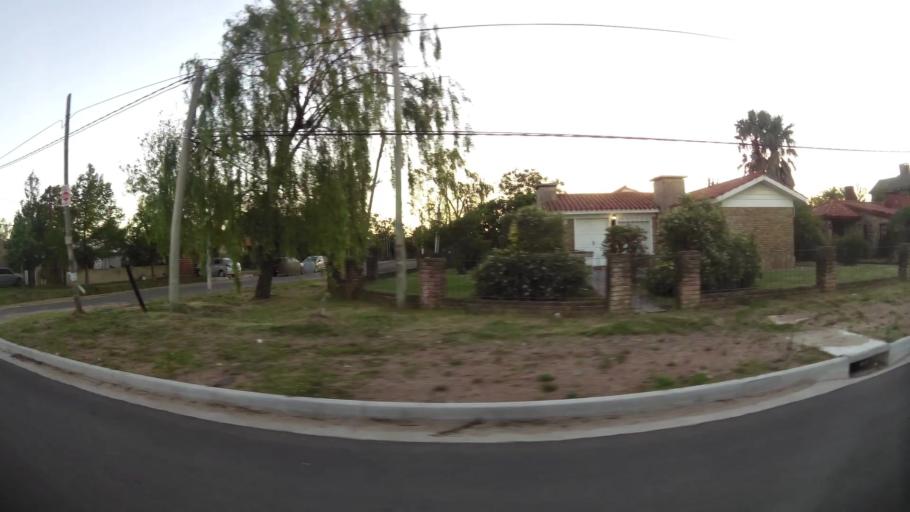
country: UY
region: Canelones
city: Barra de Carrasco
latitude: -34.8336
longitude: -55.9621
